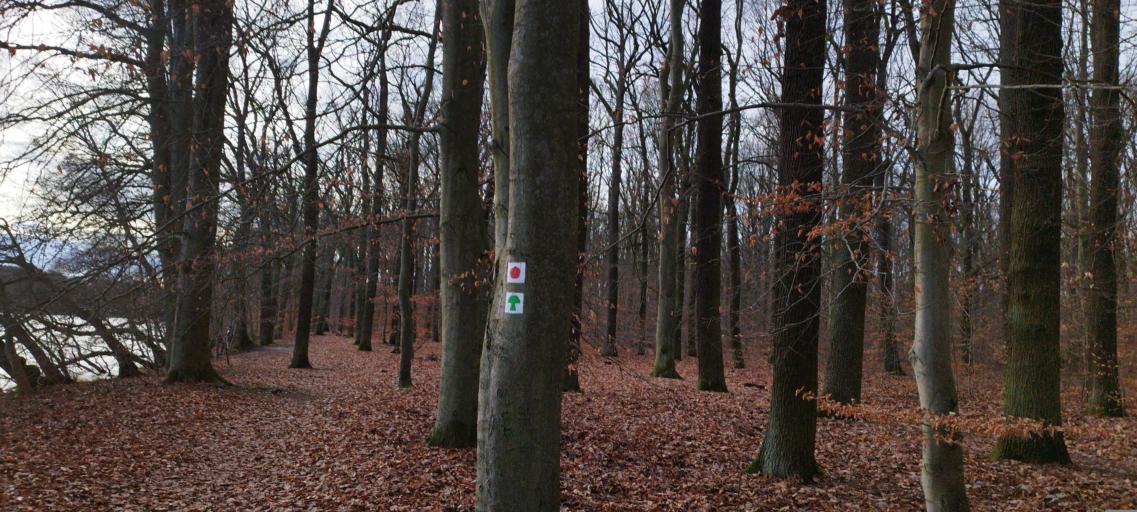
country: DE
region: Brandenburg
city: Konigs Wusterhausen
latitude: 52.2916
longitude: 13.6575
